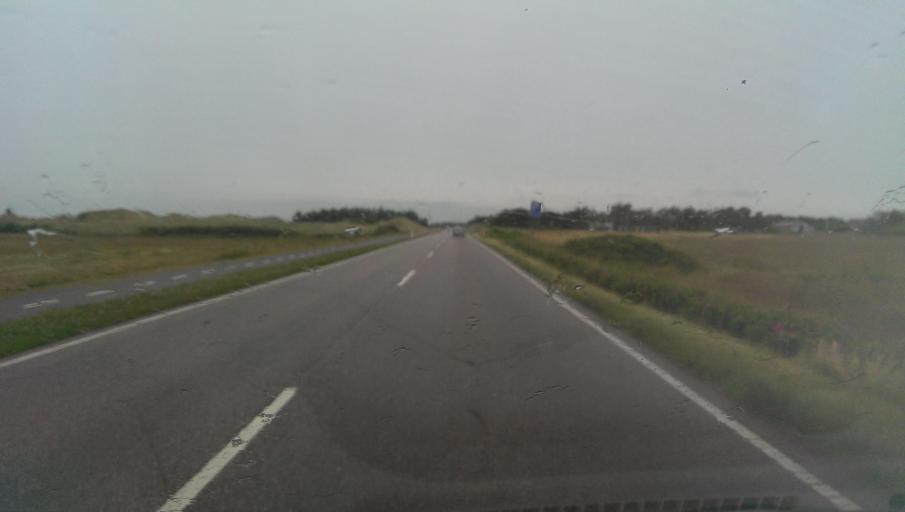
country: DK
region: Central Jutland
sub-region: Ringkobing-Skjern Kommune
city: Hvide Sande
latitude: 56.0573
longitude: 8.1209
